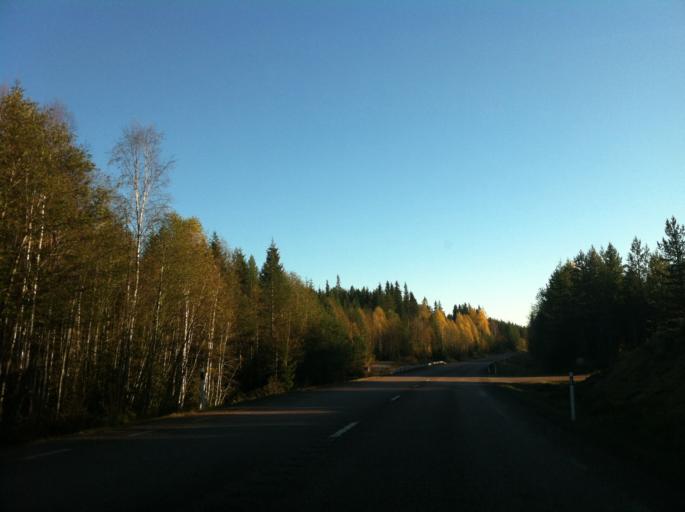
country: SE
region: Dalarna
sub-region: Faluns Kommun
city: Bjursas
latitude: 60.7812
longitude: 15.3128
